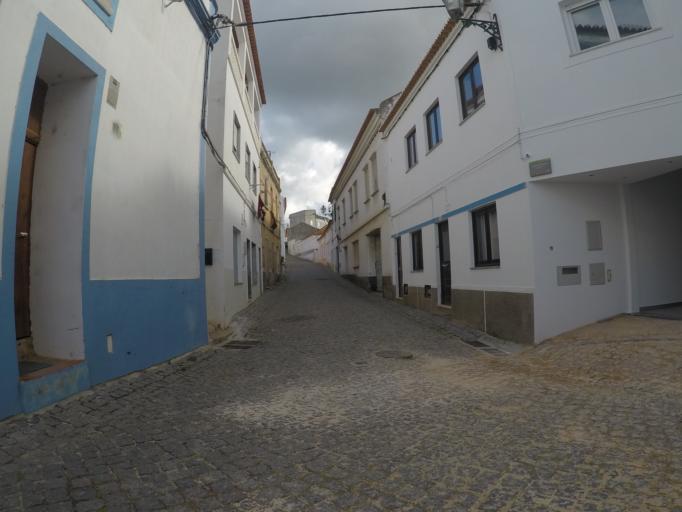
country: PT
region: Faro
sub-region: Aljezur
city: Aljezur
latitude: 37.3176
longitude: -8.8034
